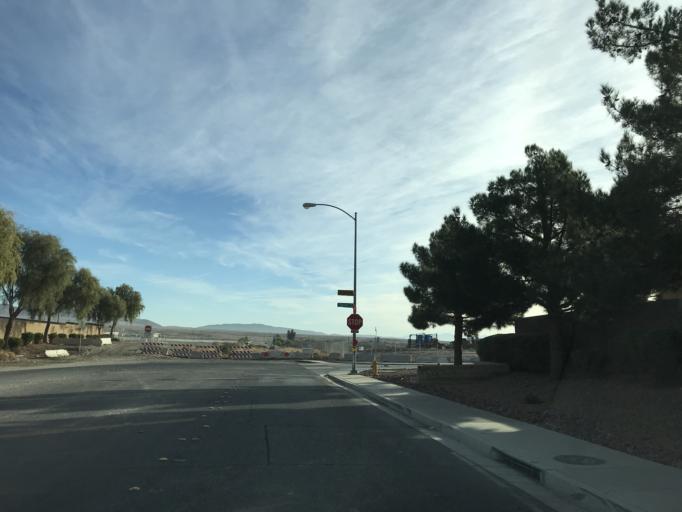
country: US
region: Nevada
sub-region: Clark County
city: Whitney
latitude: 36.1295
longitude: -115.0390
